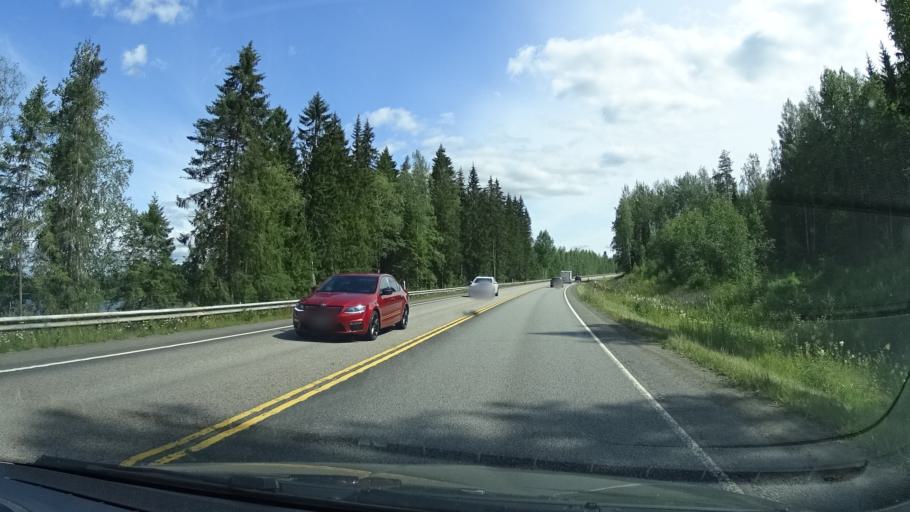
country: FI
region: Central Finland
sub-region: Jyvaeskylae
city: Jyvaeskylae
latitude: 62.2695
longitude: 25.5411
